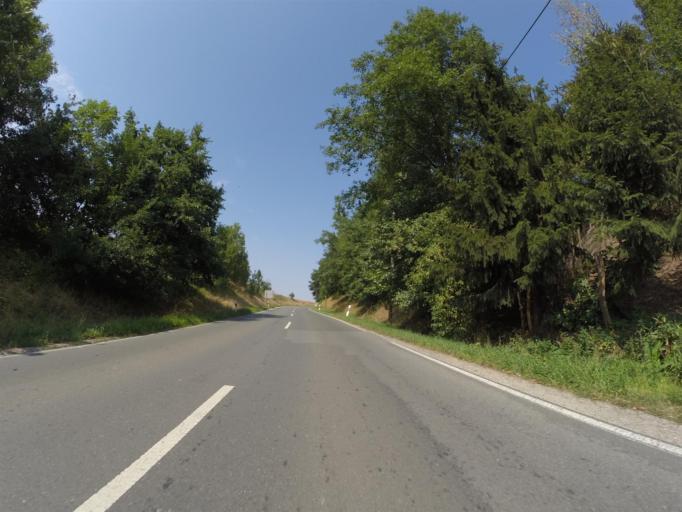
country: DE
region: Thuringia
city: Rausdorf
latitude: 50.8703
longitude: 11.6946
